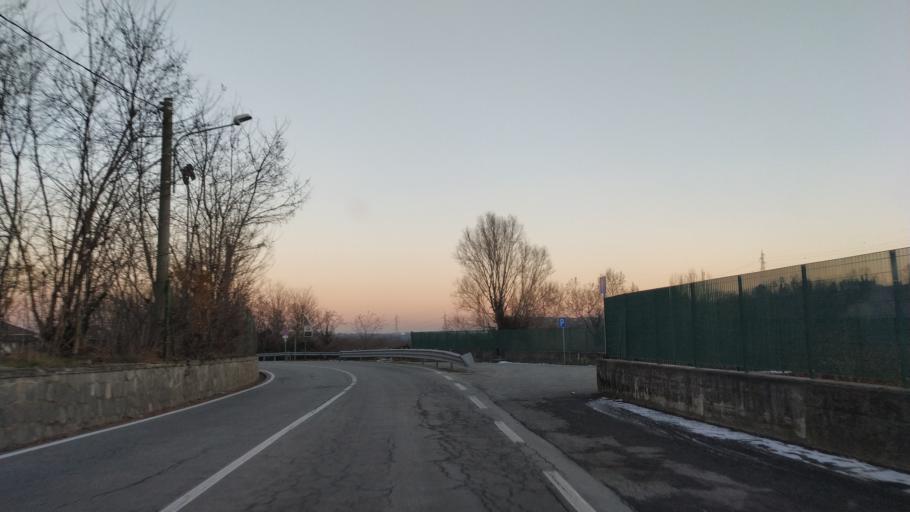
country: IT
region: Piedmont
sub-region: Provincia di Biella
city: Vigliano Biellese
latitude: 45.5575
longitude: 8.0974
